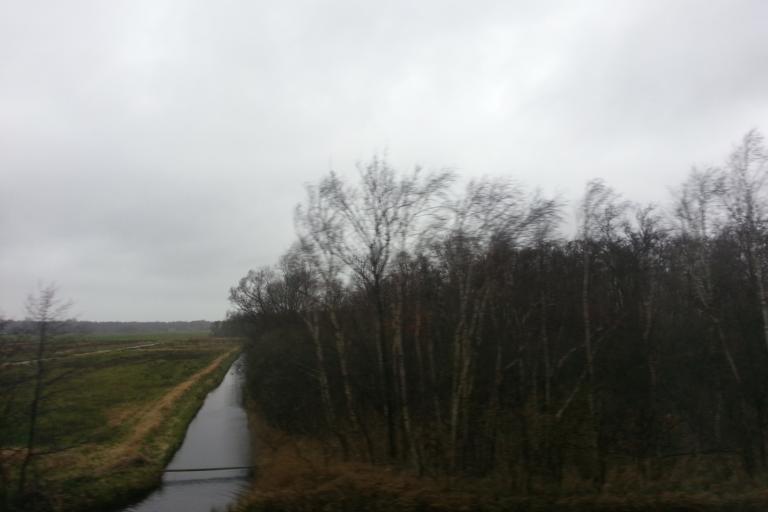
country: NL
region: South Holland
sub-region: Gemeente Leidschendam-Voorburg
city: Voorburg
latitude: 52.0994
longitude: 4.3889
